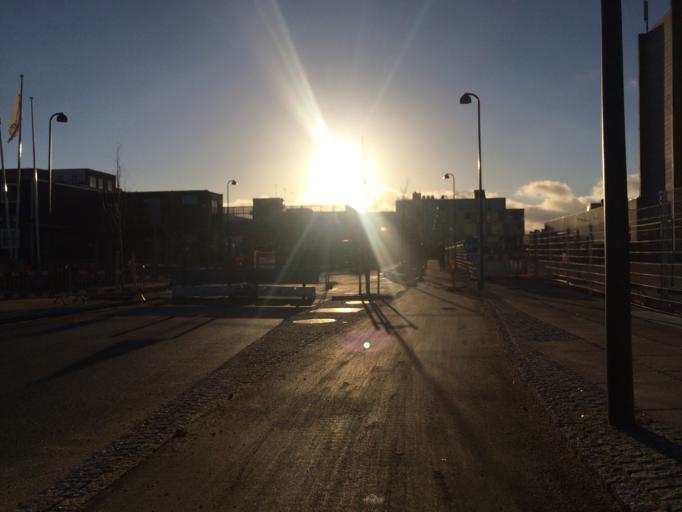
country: DK
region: Capital Region
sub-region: Kobenhavn
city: Copenhagen
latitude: 55.6528
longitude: 12.5555
